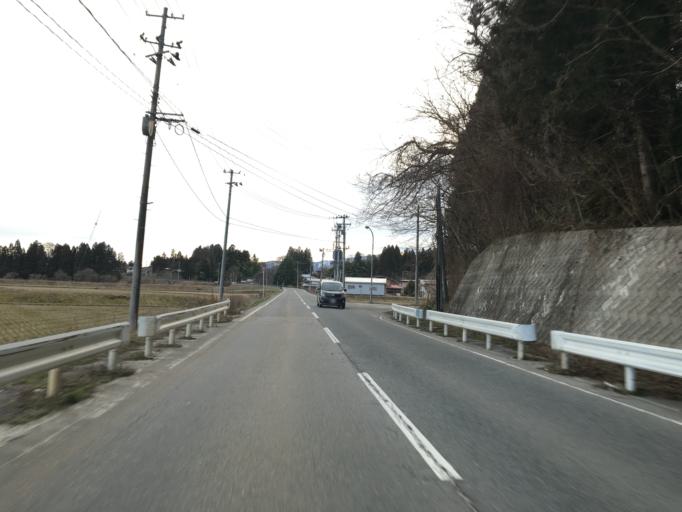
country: JP
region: Yamagata
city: Nagai
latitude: 38.1708
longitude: 140.0604
